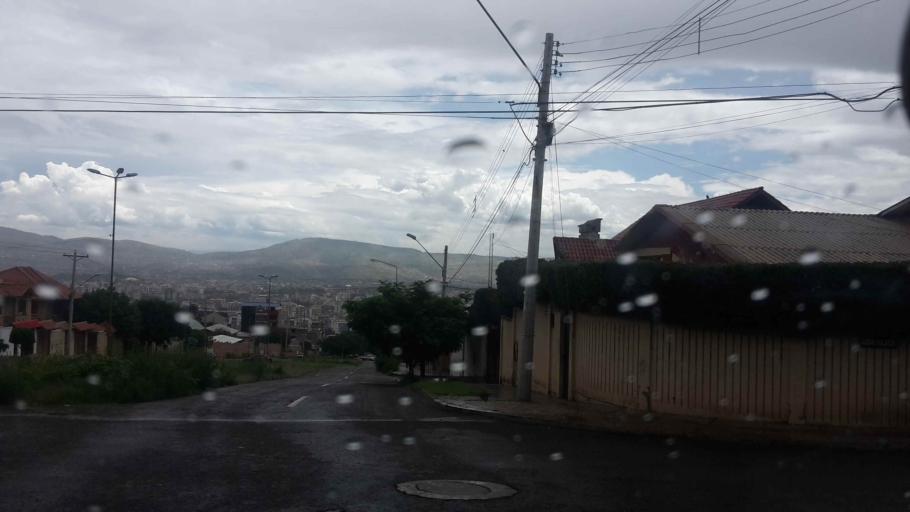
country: BO
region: Cochabamba
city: Cochabamba
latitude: -17.3588
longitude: -66.1585
